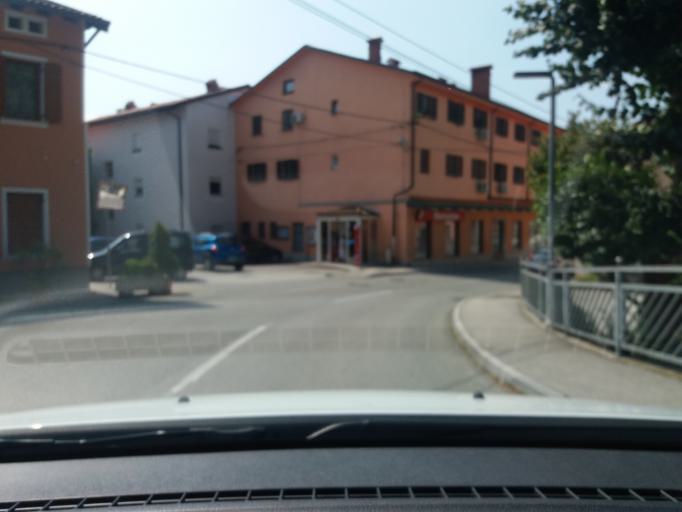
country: SI
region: Miren-Kostanjevica
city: Miren
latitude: 45.8939
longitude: 13.6084
